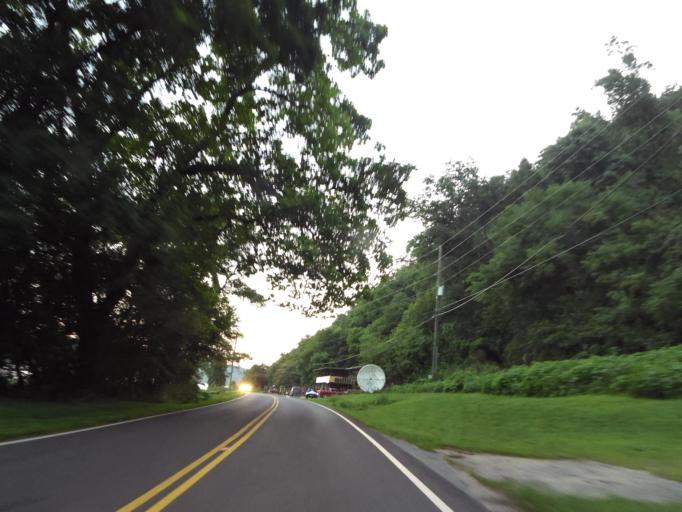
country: US
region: Tennessee
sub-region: Loudon County
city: Greenback
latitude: 35.5474
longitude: -84.0695
